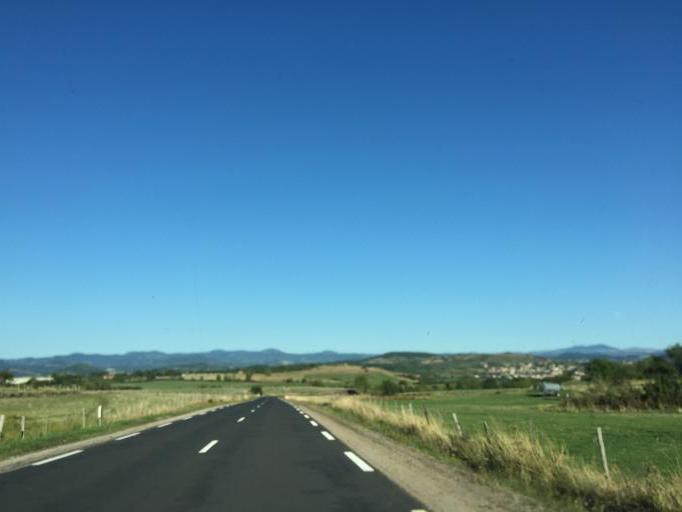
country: FR
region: Auvergne
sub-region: Departement de la Haute-Loire
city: Espaly-Saint-Marcel
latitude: 45.0341
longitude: 3.8544
